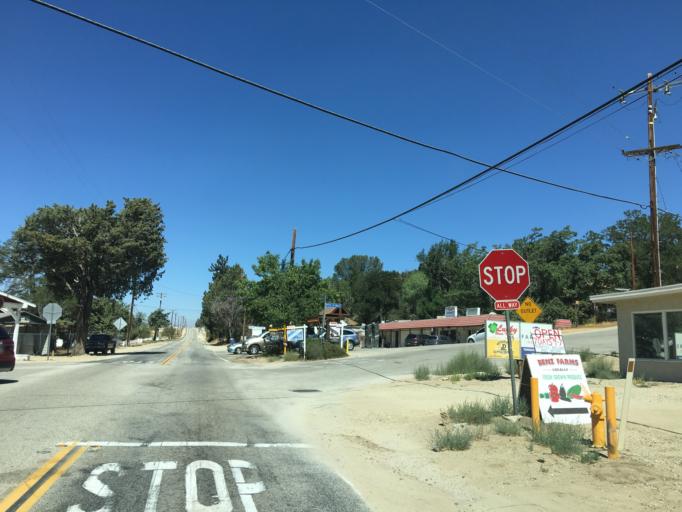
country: US
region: California
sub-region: Los Angeles County
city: Leona Valley
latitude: 34.6180
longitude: -118.2883
